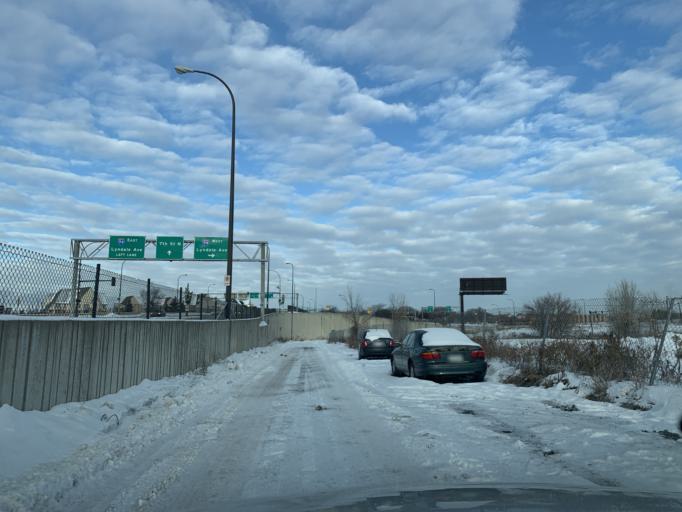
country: US
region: Minnesota
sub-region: Hennepin County
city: Minneapolis
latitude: 44.9866
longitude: -93.2868
